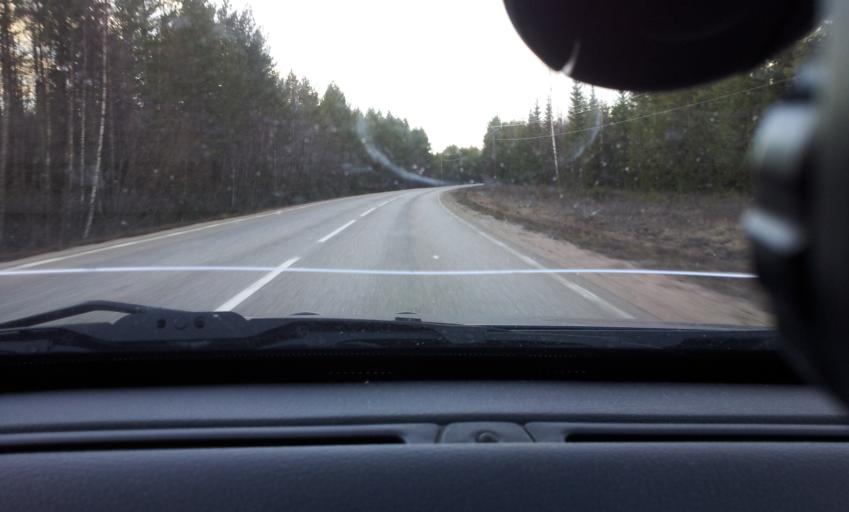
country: SE
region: Vaesternorrland
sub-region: Ange Kommun
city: Ange
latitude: 62.0833
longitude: 15.0961
